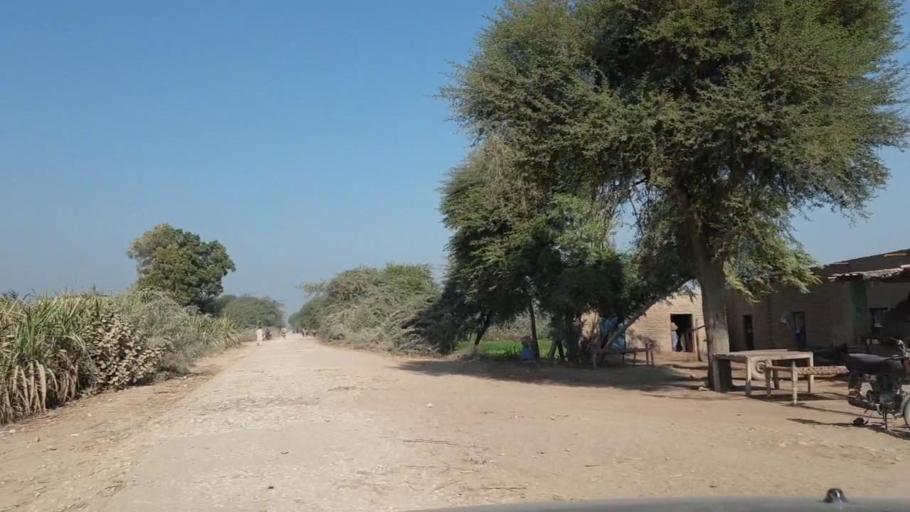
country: PK
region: Sindh
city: Tando Allahyar
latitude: 25.5704
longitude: 68.6077
